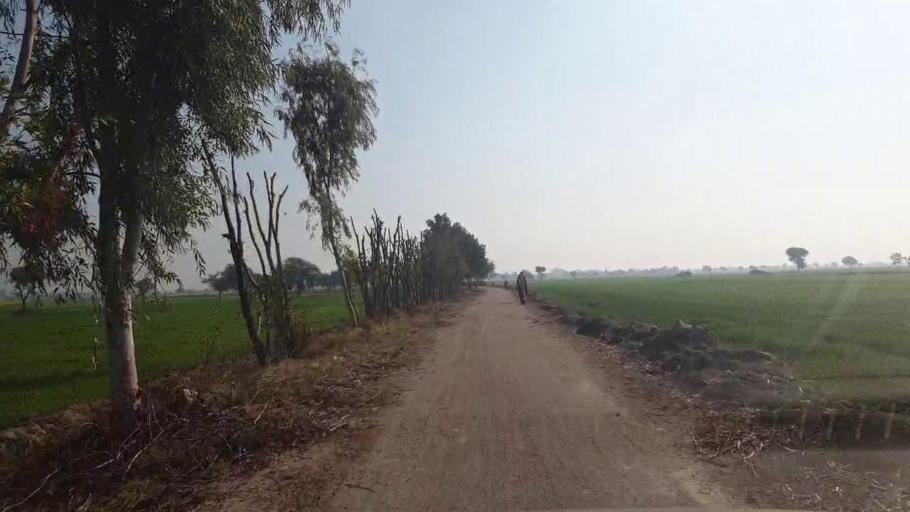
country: PK
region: Sindh
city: Shahdadpur
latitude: 25.9754
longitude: 68.5915
